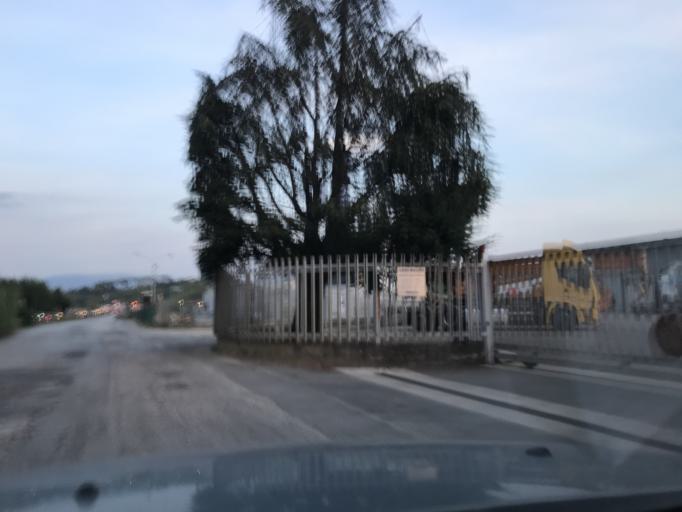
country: IT
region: Umbria
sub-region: Provincia di Perugia
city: Via Lippia
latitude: 43.0887
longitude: 12.4580
